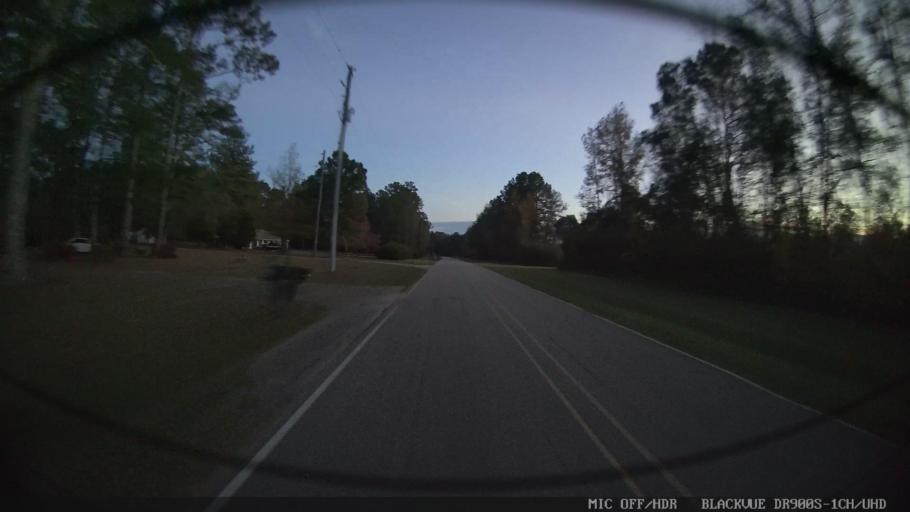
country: US
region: Mississippi
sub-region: Perry County
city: New Augusta
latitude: 31.1597
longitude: -89.2118
